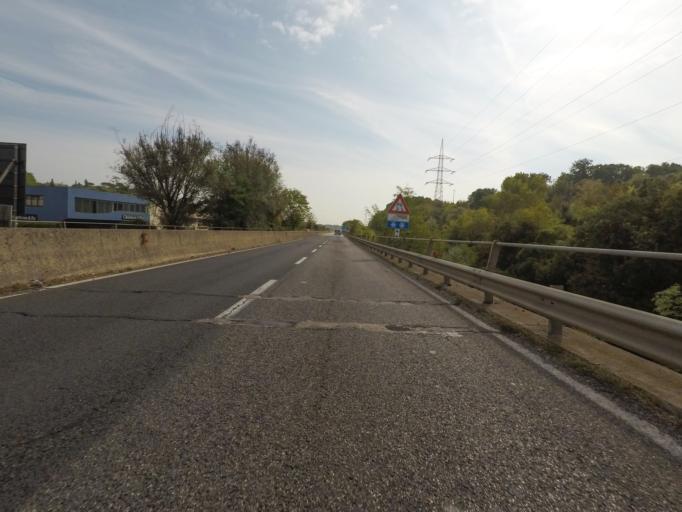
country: IT
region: Tuscany
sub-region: Provincia di Siena
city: Siena
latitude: 43.3056
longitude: 11.3170
